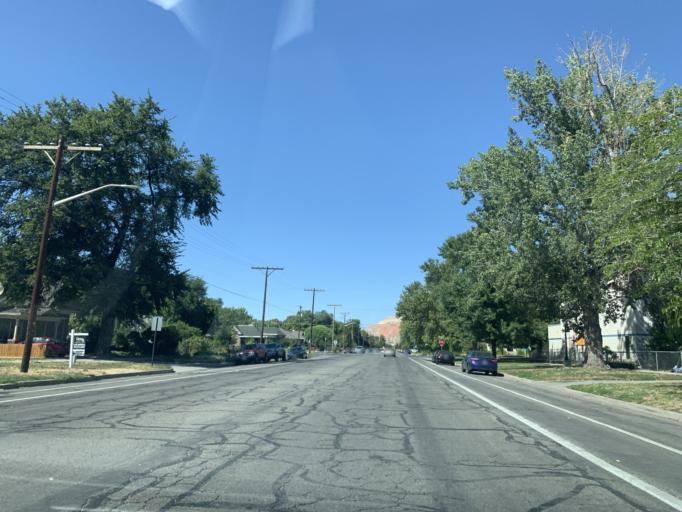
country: US
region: Utah
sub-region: Salt Lake County
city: Salt Lake City
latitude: 40.7749
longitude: -111.9082
